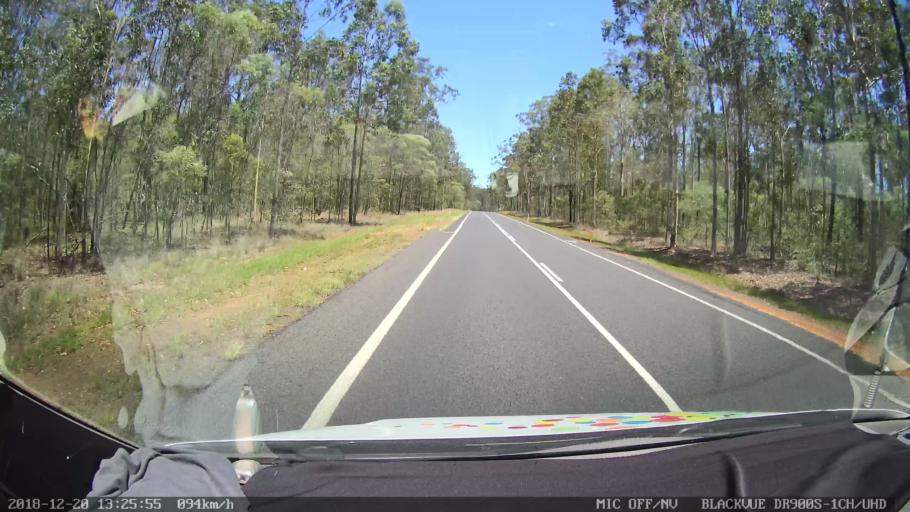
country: AU
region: New South Wales
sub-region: Richmond Valley
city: Casino
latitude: -29.1381
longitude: 152.9960
